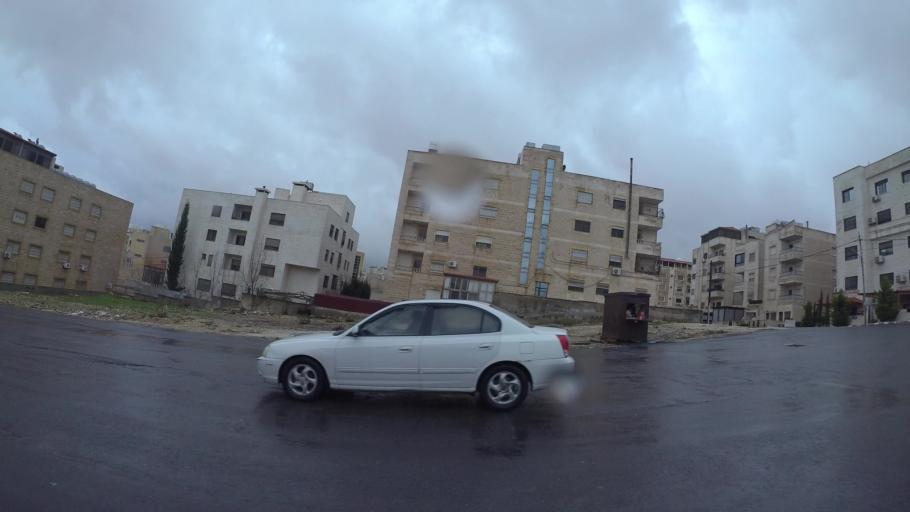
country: JO
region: Amman
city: Al Jubayhah
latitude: 32.0340
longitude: 35.8874
